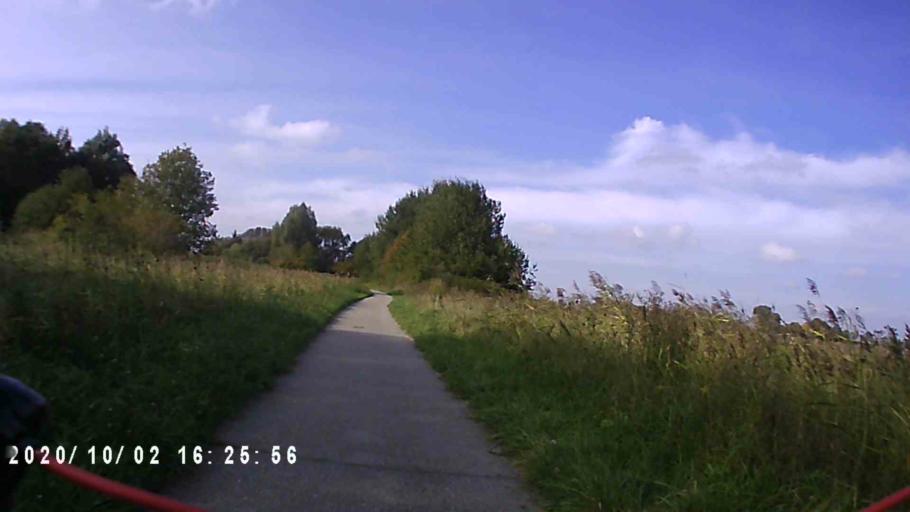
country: NL
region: Groningen
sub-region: Gemeente Zuidhorn
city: Grijpskerk
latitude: 53.2850
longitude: 6.3129
